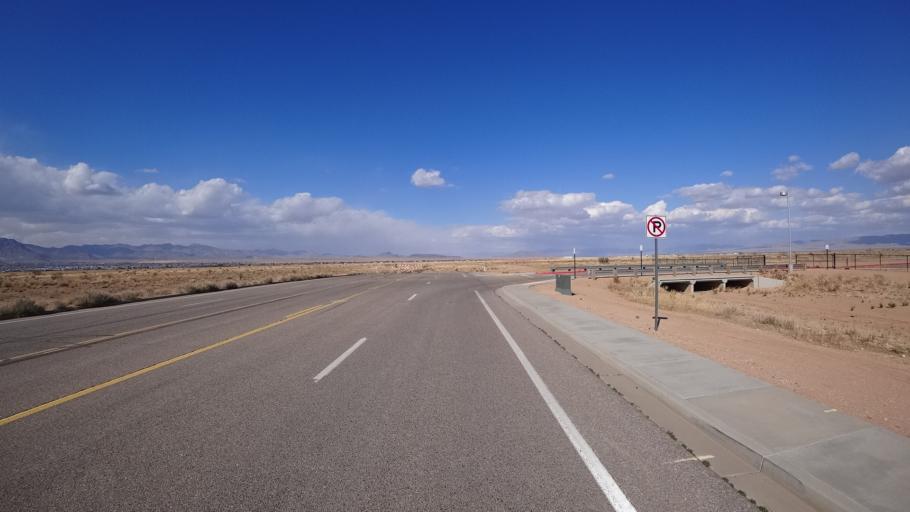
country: US
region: Arizona
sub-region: Mohave County
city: New Kingman-Butler
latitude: 35.2298
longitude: -113.9756
